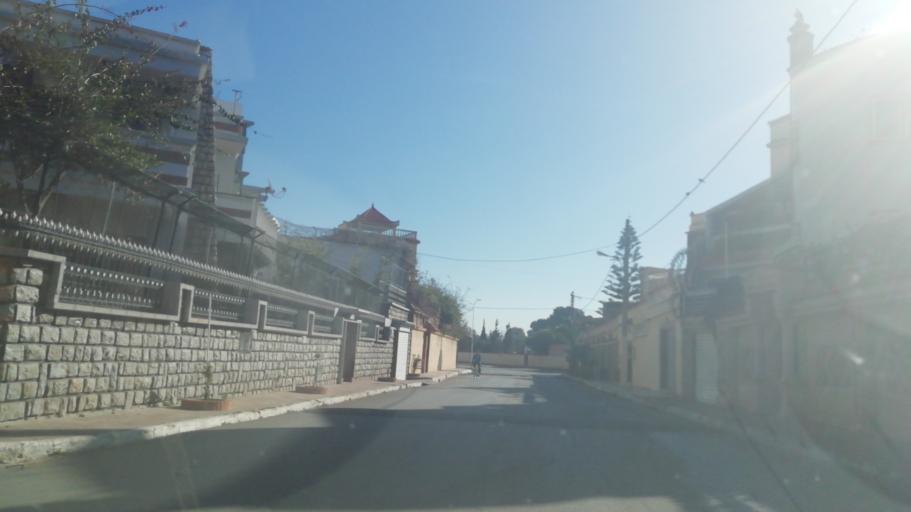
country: DZ
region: Oran
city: Oran
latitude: 35.6750
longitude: -0.6345
